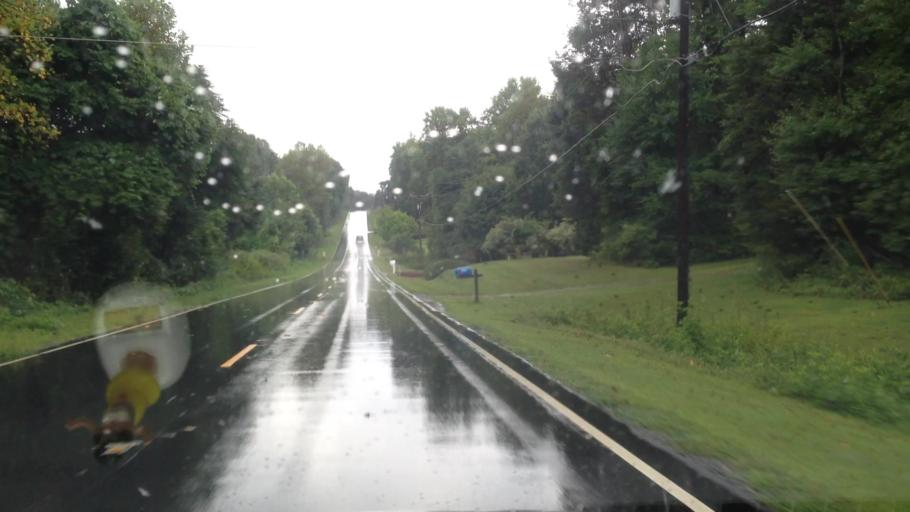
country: US
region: North Carolina
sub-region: Rockingham County
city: Mayodan
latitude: 36.4179
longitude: -80.0852
